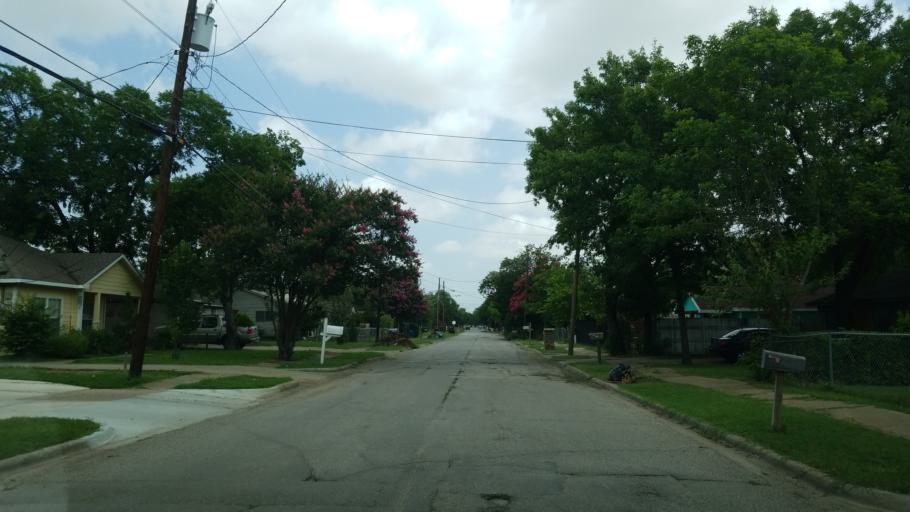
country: US
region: Texas
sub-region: Dallas County
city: Cockrell Hill
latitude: 32.7874
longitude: -96.9024
